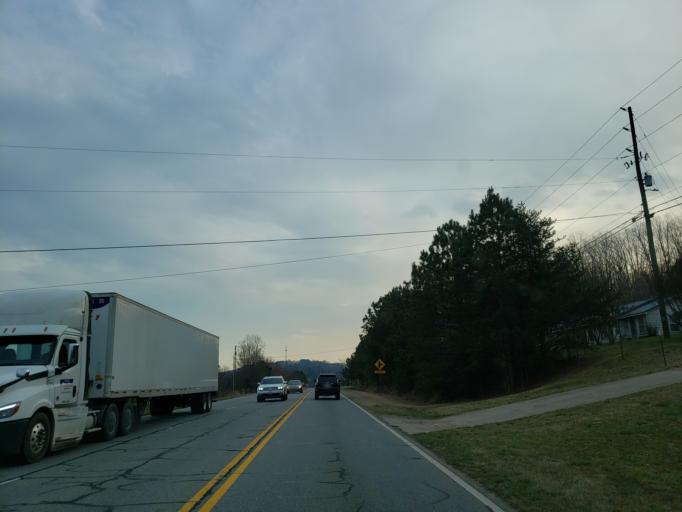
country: US
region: Georgia
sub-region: Whitfield County
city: Varnell
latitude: 34.8680
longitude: -85.0176
